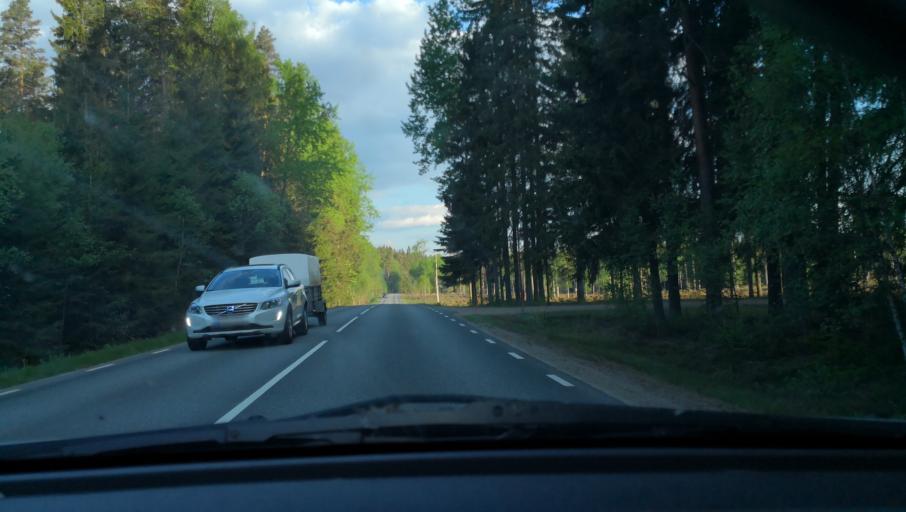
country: SE
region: Joenkoeping
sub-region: Vetlanda Kommun
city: Landsbro
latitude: 57.3871
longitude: 14.8381
